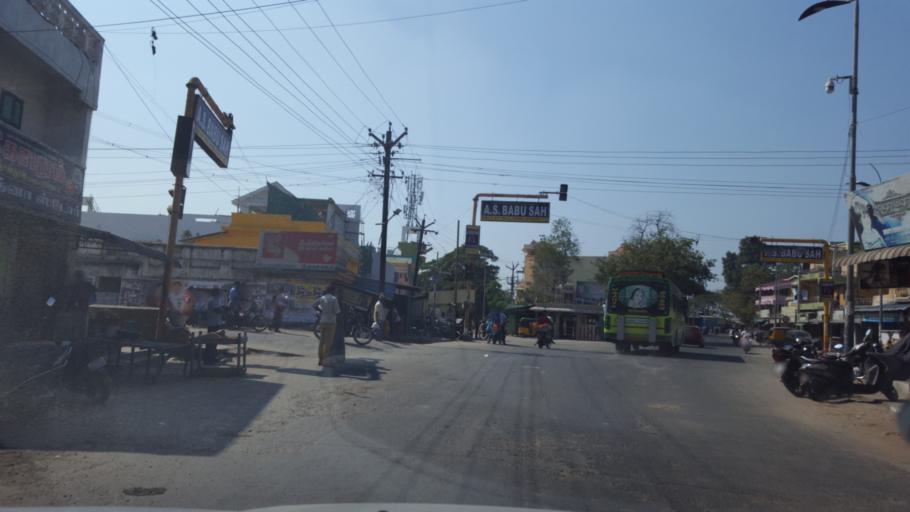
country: IN
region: Tamil Nadu
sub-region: Kancheepuram
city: Kanchipuram
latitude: 12.8448
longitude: 79.6969
